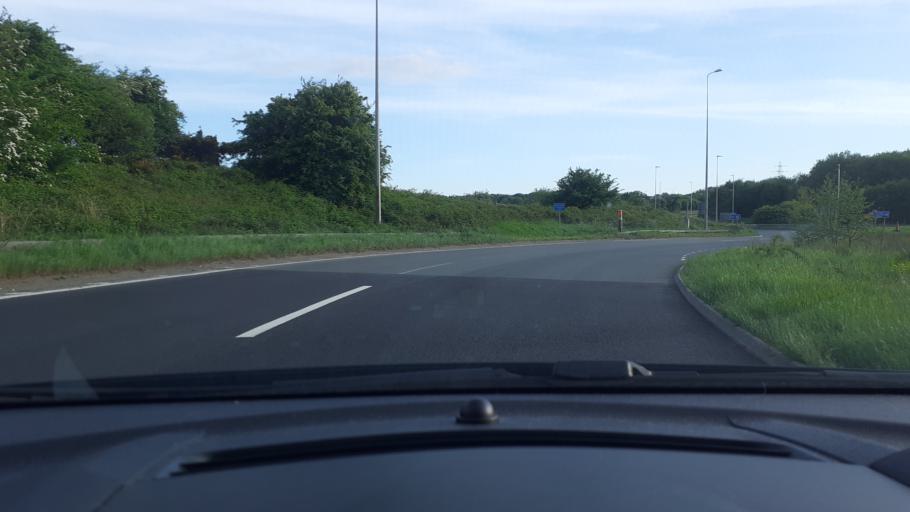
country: GB
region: England
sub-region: Borough of Wigan
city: Shevington
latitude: 53.5343
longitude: -2.6945
